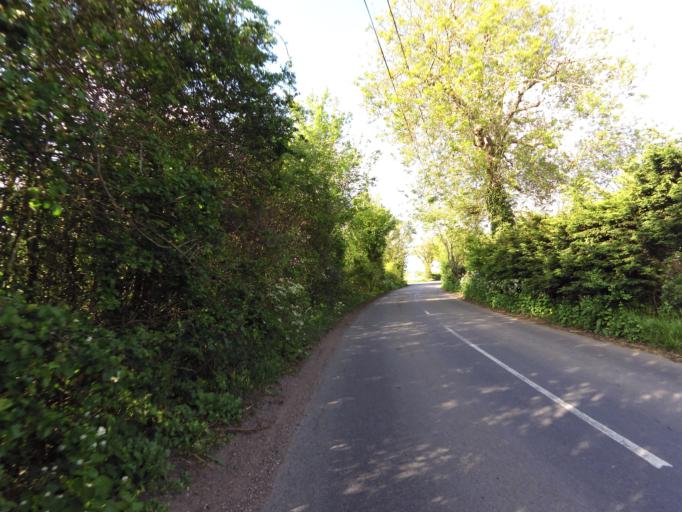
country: GB
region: England
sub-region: Suffolk
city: Halesworth
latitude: 52.4012
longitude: 1.5211
